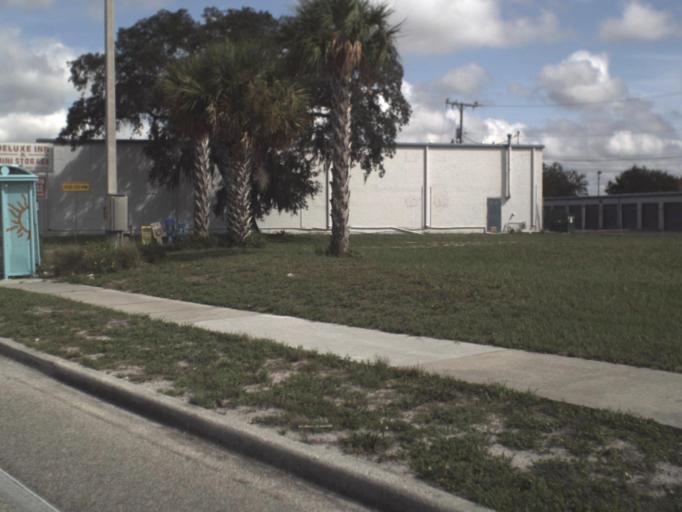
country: US
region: Florida
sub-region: Manatee County
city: Whitfield
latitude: 27.3961
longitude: -82.5630
